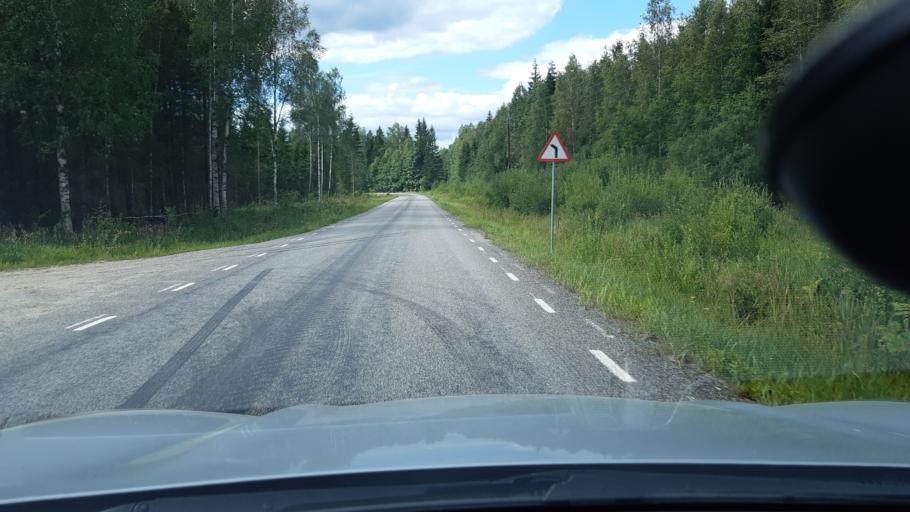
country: EE
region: Raplamaa
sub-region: Jaervakandi vald
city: Jarvakandi
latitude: 58.7988
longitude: 24.8754
